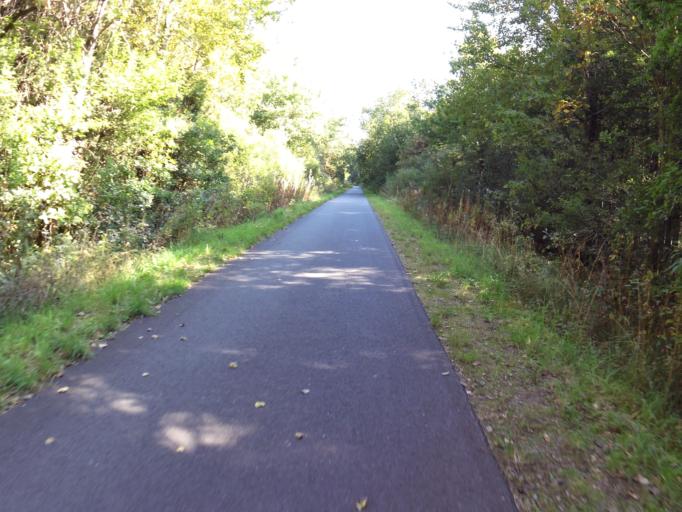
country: BE
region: Wallonia
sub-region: Province de Liege
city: Butgenbach
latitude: 50.4072
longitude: 6.1679
